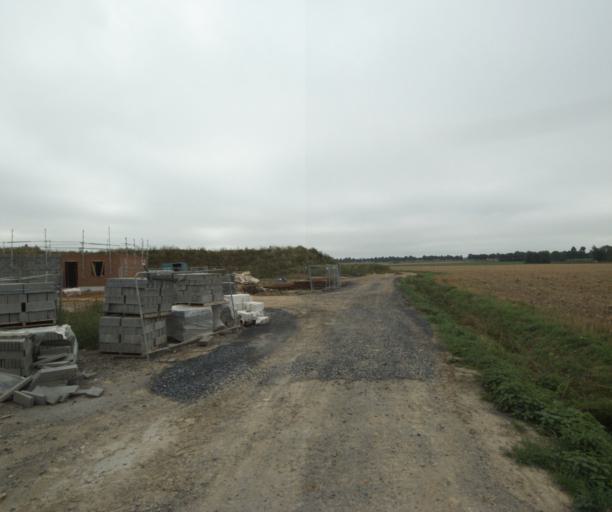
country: FR
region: Nord-Pas-de-Calais
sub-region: Departement du Nord
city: Willems
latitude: 50.6143
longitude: 3.2326
